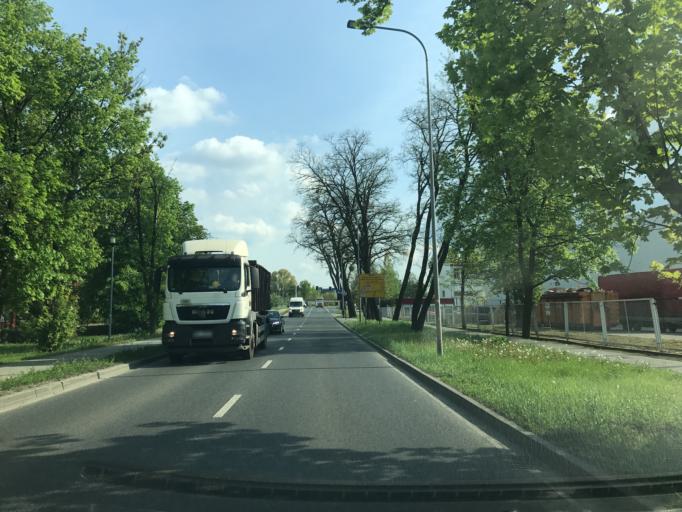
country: PL
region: Kujawsko-Pomorskie
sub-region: Powiat bydgoski
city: Osielsko
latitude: 53.1202
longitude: 18.0874
